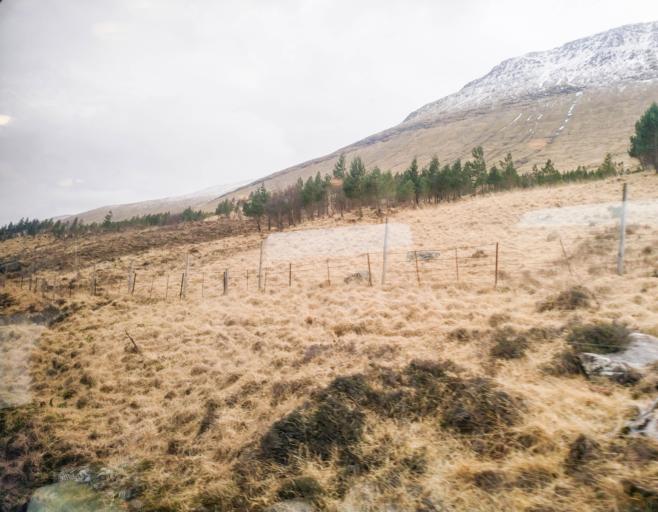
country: GB
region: Scotland
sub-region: Highland
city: Spean Bridge
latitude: 56.5603
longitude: -4.7161
